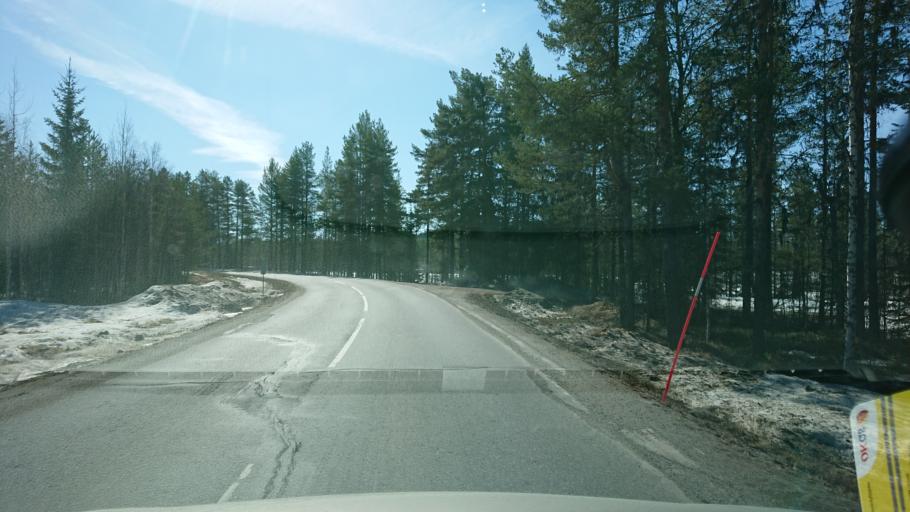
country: SE
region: Vaesterbotten
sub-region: Dorotea Kommun
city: Dorotea
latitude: 64.0102
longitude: 16.2948
